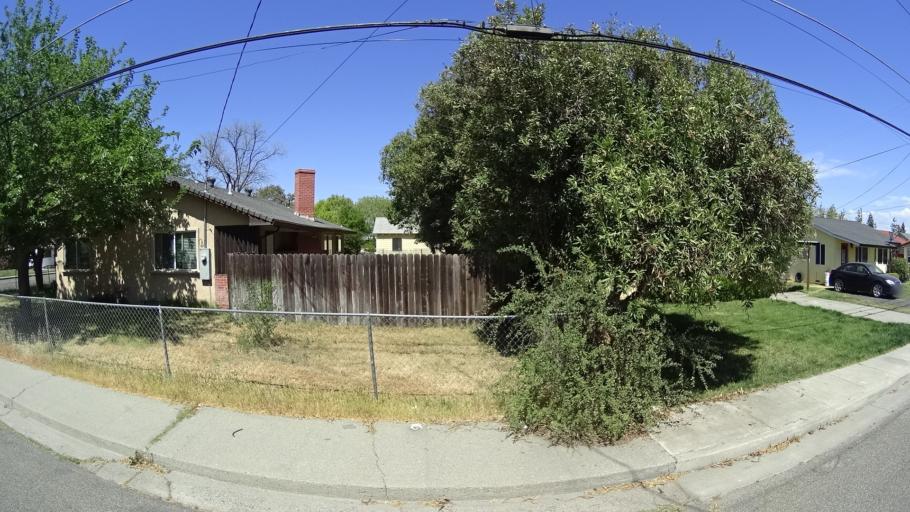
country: US
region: California
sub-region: Glenn County
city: Orland
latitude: 39.7401
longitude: -122.1857
